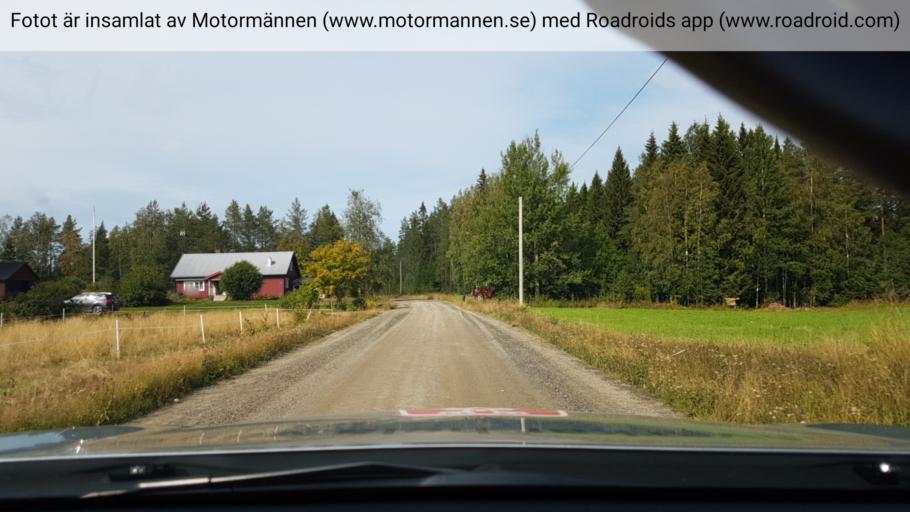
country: SE
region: Vaesterbotten
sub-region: Vannas Kommun
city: Vaennaes
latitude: 63.9521
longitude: 19.5644
